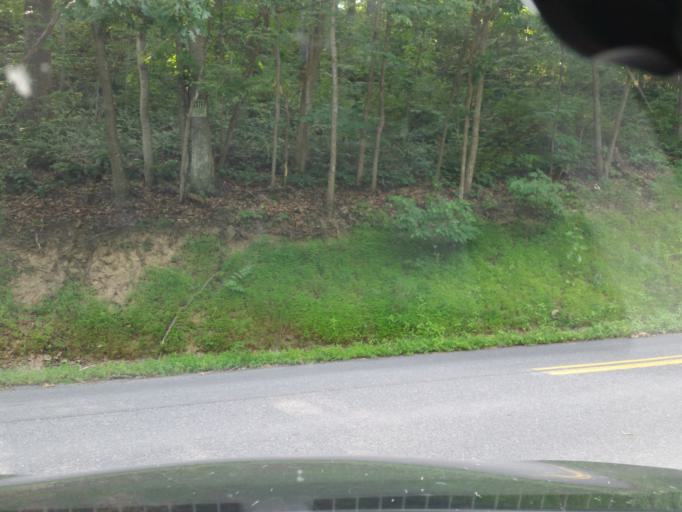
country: US
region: Pennsylvania
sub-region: Union County
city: New Columbia
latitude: 41.0257
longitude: -76.9111
